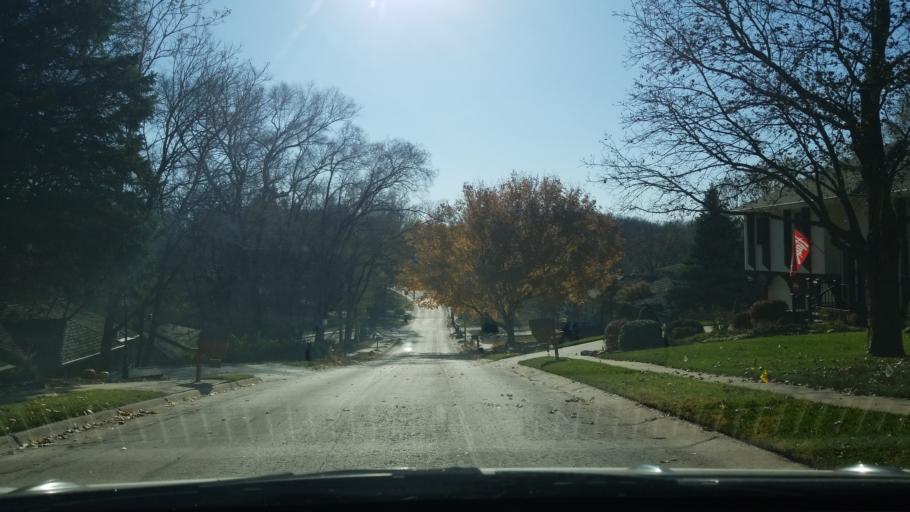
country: US
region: Nebraska
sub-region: Sarpy County
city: Bellevue
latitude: 41.1630
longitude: -95.9010
